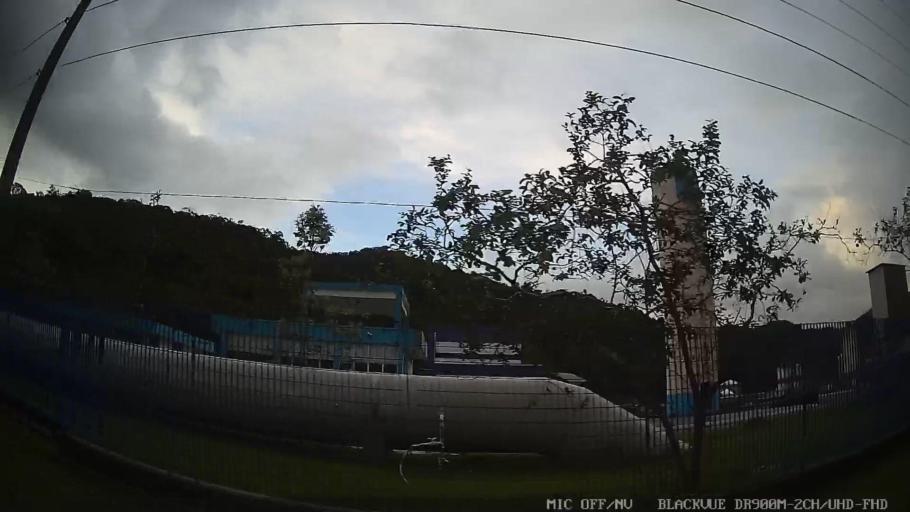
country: BR
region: Sao Paulo
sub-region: Itanhaem
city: Itanhaem
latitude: -24.0868
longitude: -46.7984
